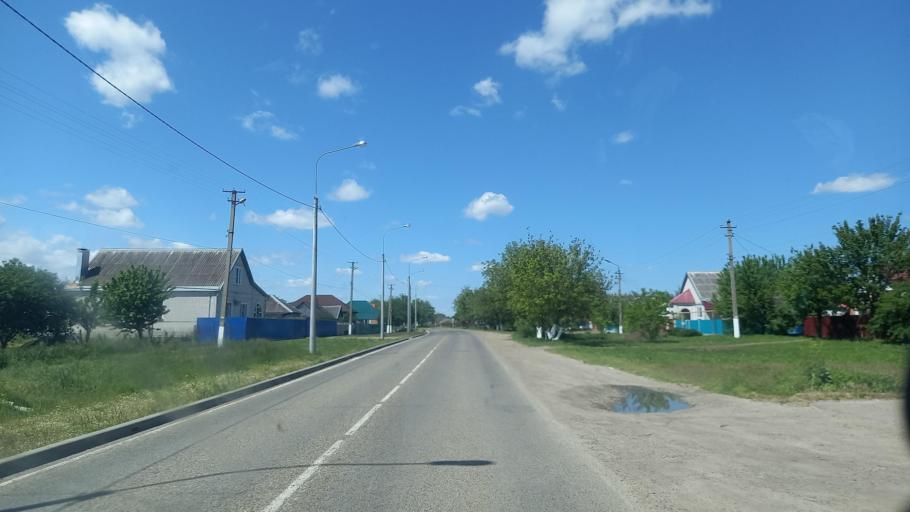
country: RU
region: Krasnodarskiy
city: Novoukrainskoye
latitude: 45.3806
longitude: 40.5010
